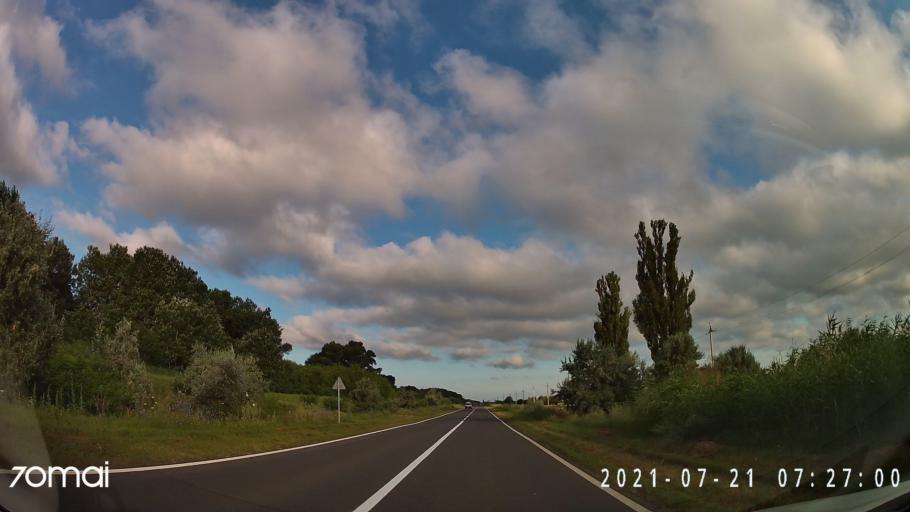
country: RO
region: Tulcea
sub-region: Oras Isaccea
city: Isaccea
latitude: 45.3008
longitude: 28.4267
